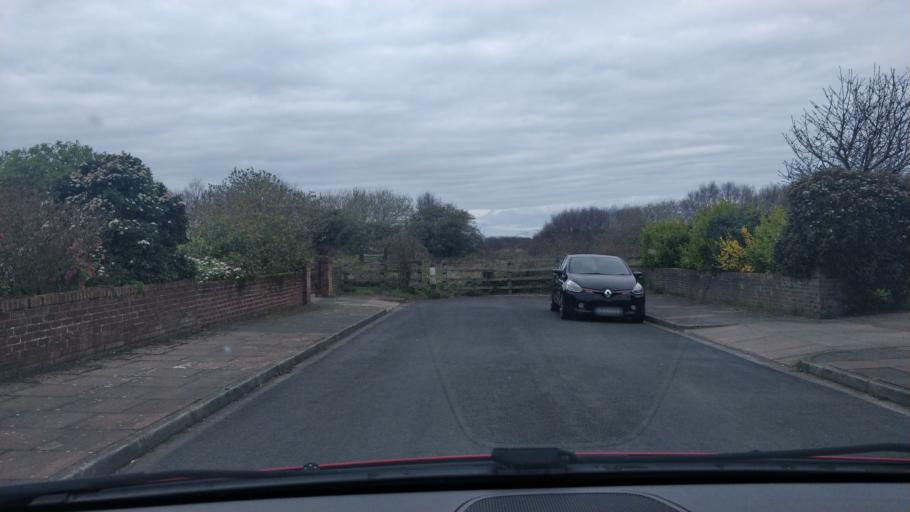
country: GB
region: England
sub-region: Sefton
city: Formby
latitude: 53.6066
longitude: -3.0516
